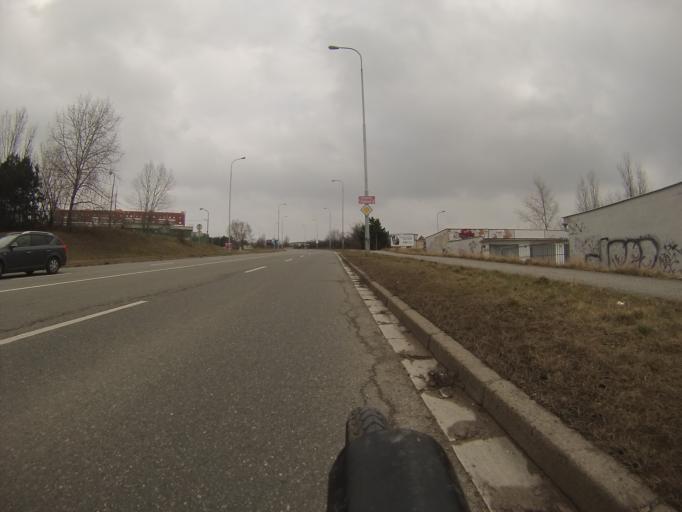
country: CZ
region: South Moravian
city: Bilovice nad Svitavou
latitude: 49.2030
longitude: 16.6763
